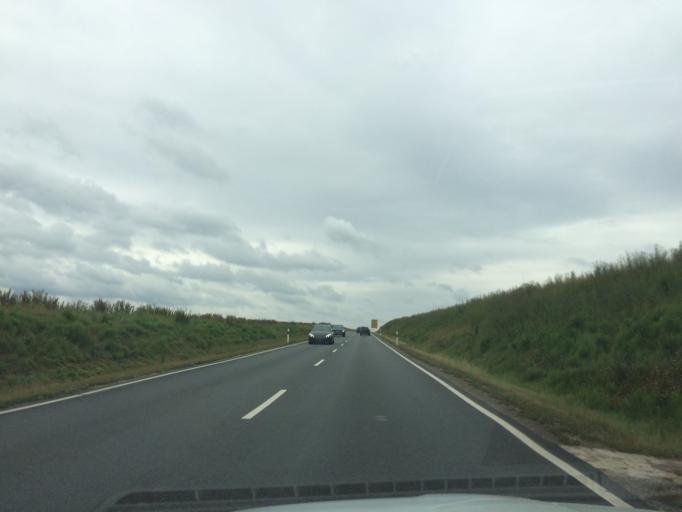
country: DE
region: Hesse
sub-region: Regierungsbezirk Kassel
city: Hofgeismar
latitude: 51.4989
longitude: 9.4060
